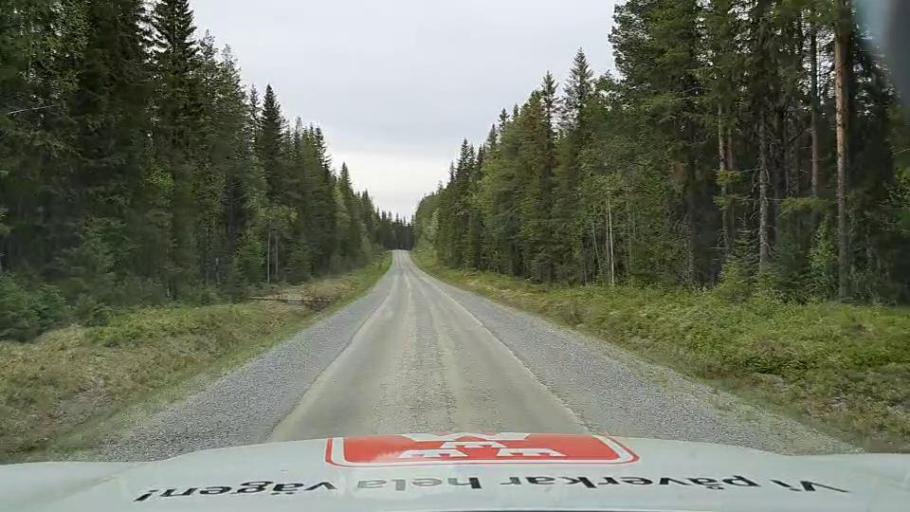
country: SE
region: Jaemtland
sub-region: OEstersunds Kommun
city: Brunflo
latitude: 62.6331
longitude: 14.9392
